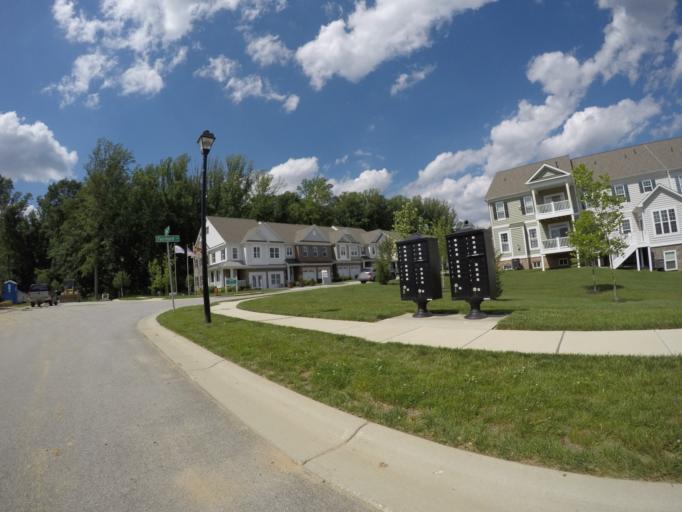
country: US
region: Maryland
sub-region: Howard County
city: Columbia
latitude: 39.3015
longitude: -76.8934
